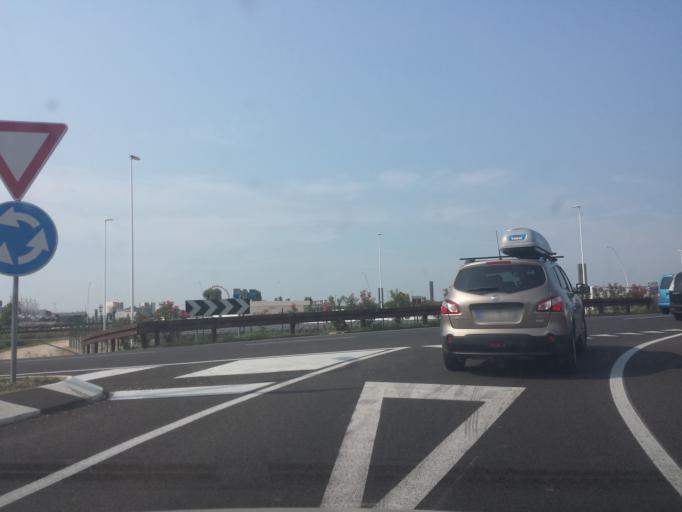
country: IT
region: Veneto
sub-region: Provincia di Venezia
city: Lido di Iesolo
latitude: 45.5106
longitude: 12.6355
